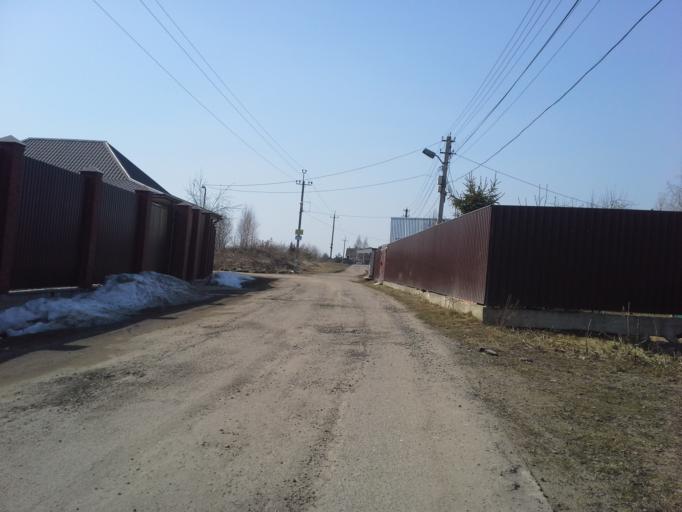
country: RU
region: Moskovskaya
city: Filimonki
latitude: 55.5452
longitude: 37.3790
